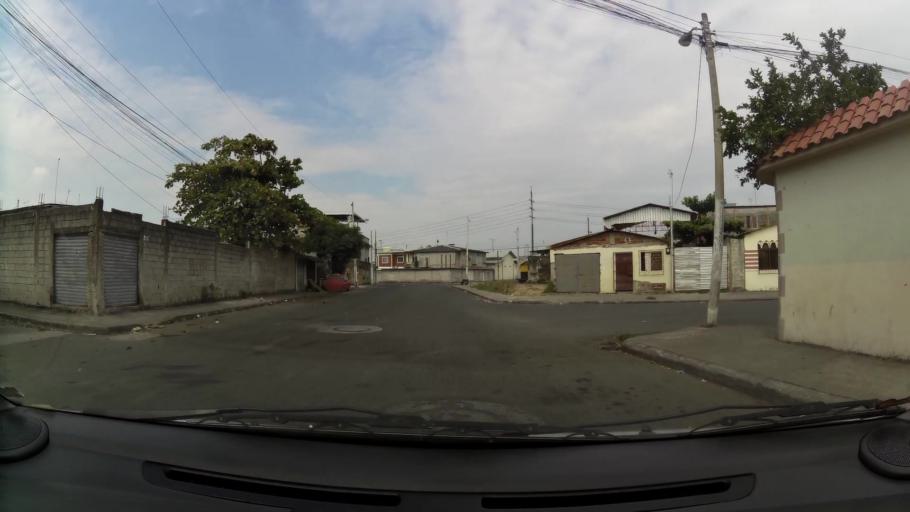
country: EC
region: Guayas
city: Guayaquil
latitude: -2.2608
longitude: -79.8976
